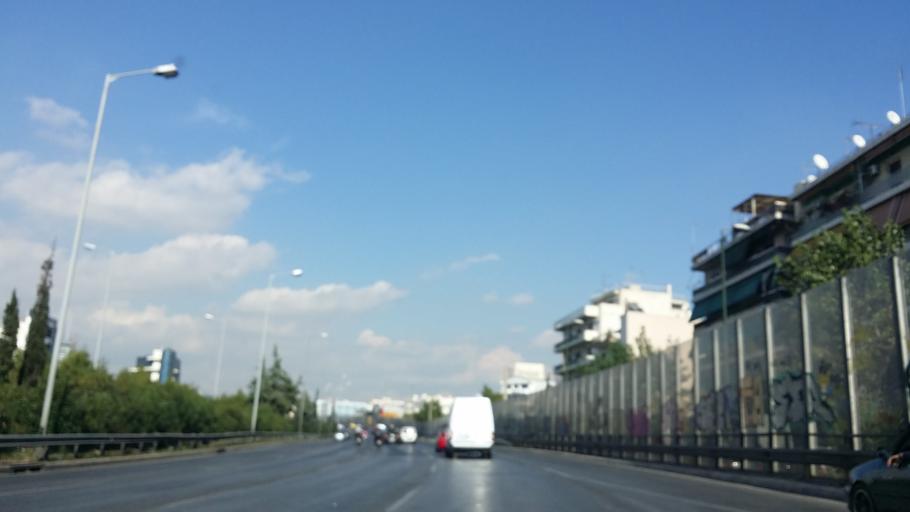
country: GR
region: Attica
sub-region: Nomarchia Athinas
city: Nea Chalkidona
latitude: 38.0189
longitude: 23.7232
